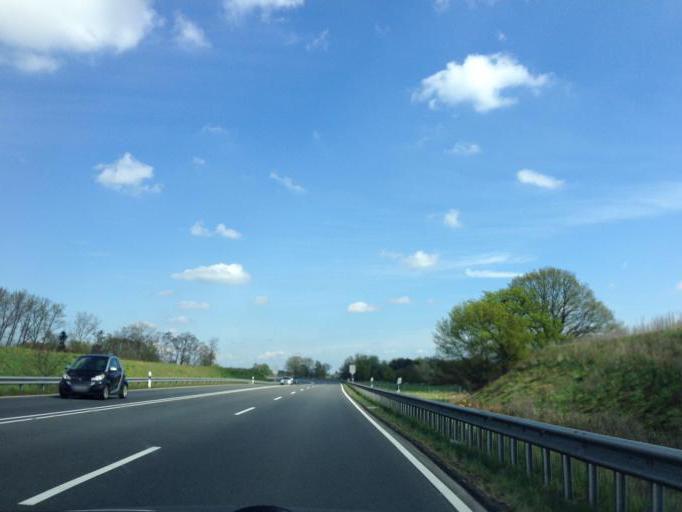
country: DE
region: Lower Saxony
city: Celle
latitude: 52.5926
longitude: 10.0776
